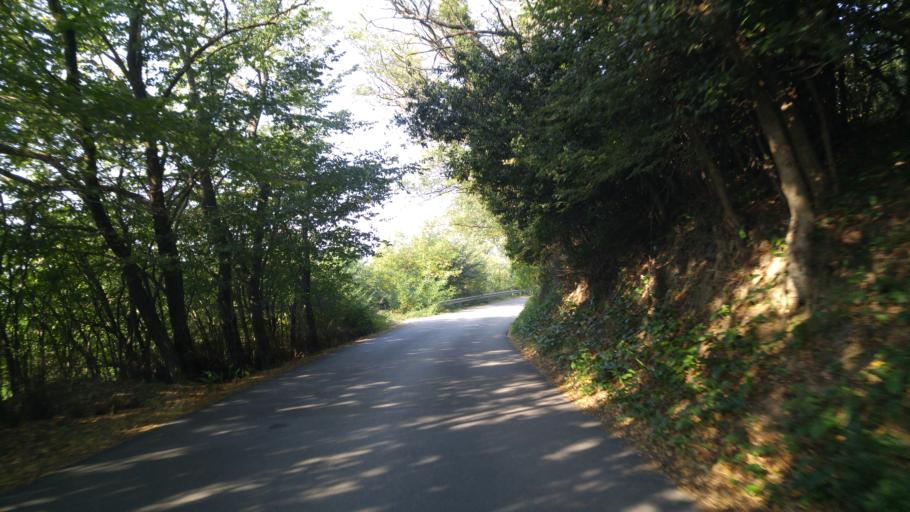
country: IT
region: The Marches
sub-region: Provincia di Pesaro e Urbino
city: Fenile
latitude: 43.8635
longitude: 12.9643
